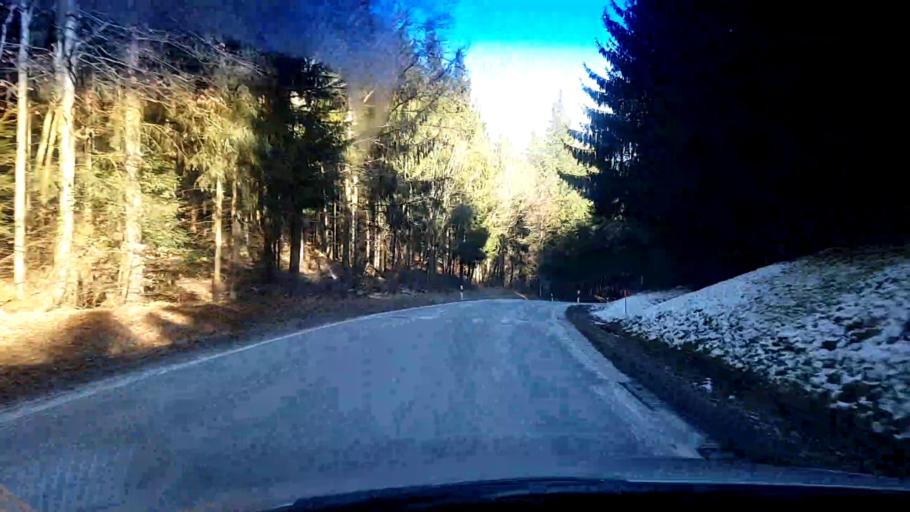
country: DE
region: Bavaria
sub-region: Upper Franconia
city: Aufsess
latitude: 49.8809
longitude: 11.2133
